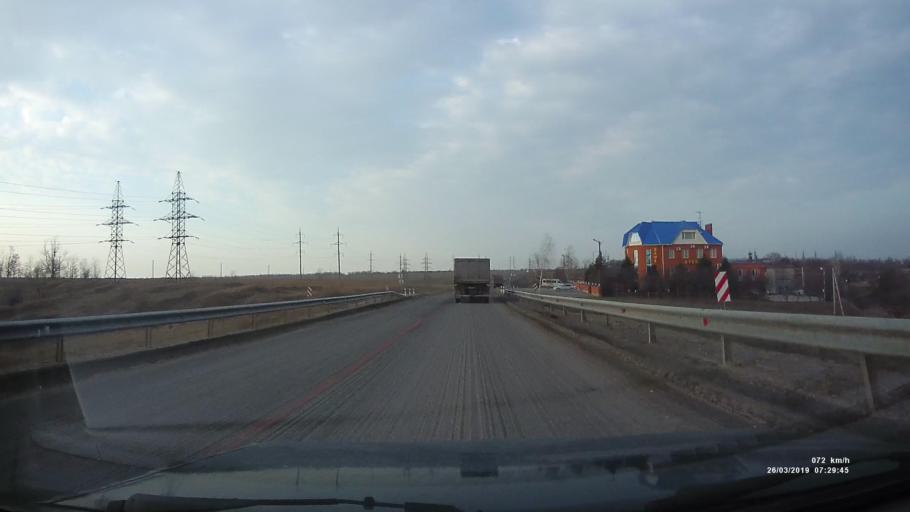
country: RU
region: Rostov
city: Novobessergenovka
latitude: 47.2422
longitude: 38.8140
